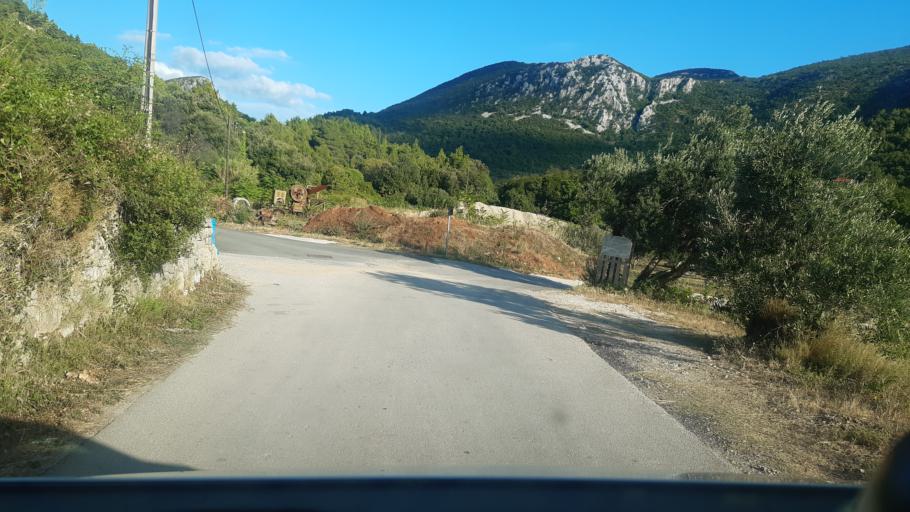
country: HR
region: Dubrovacko-Neretvanska
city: Blato
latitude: 42.8892
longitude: 17.4592
